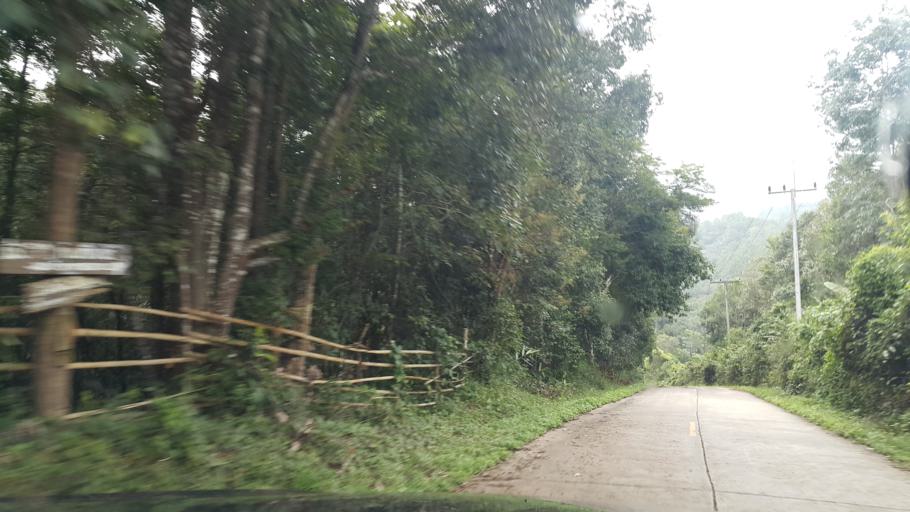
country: TH
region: Lampang
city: Wang Nuea
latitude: 19.0732
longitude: 99.3881
